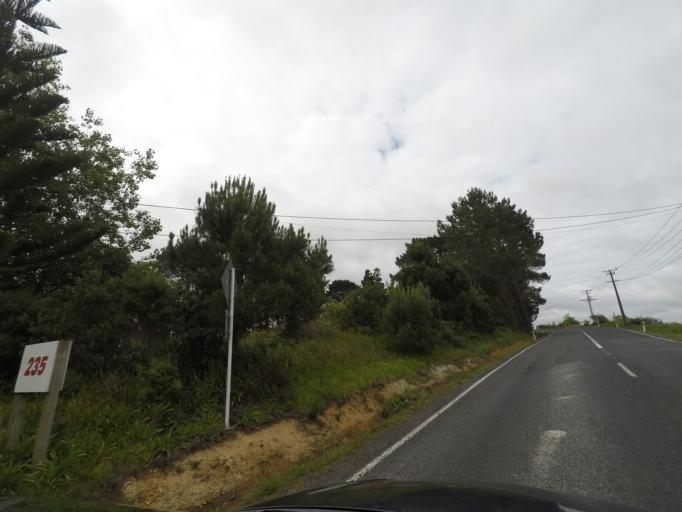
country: NZ
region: Auckland
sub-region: Auckland
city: Rosebank
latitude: -36.8302
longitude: 174.5753
